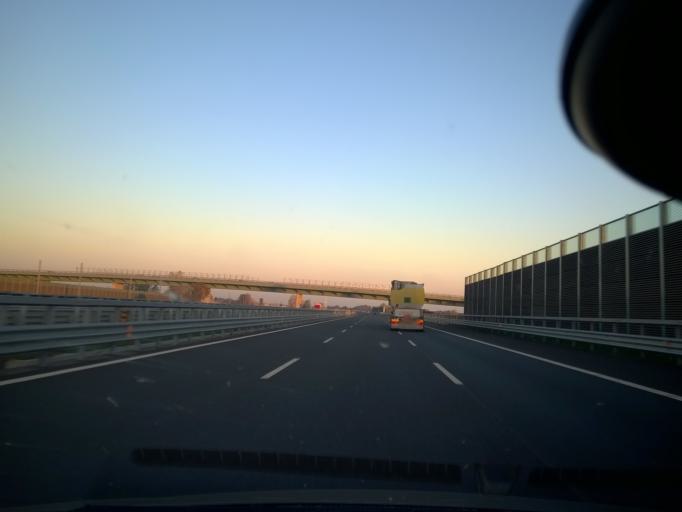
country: IT
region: Lombardy
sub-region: Provincia di Bergamo
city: Casirate d'Adda
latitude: 45.5041
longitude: 9.5781
